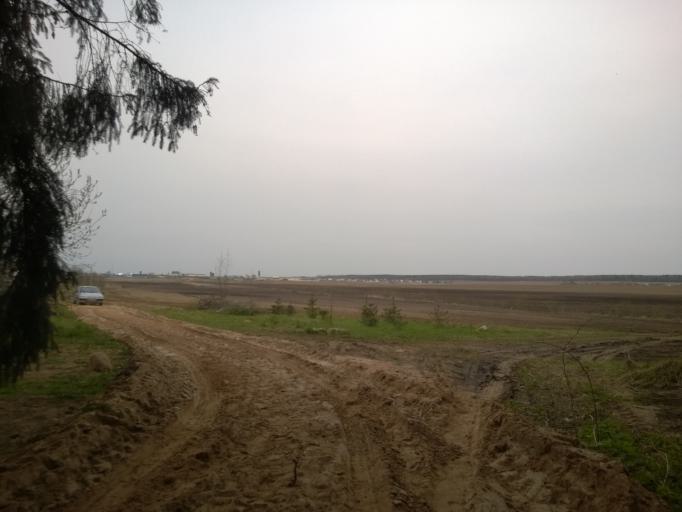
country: BY
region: Minsk
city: Slabada
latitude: 54.0043
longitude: 27.8479
